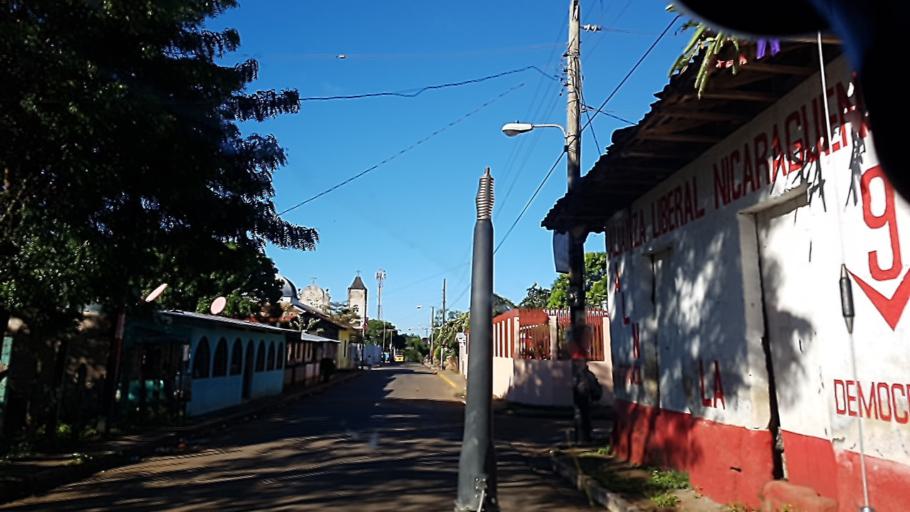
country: NI
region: Carazo
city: Santa Teresa
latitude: 11.7350
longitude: -86.1915
